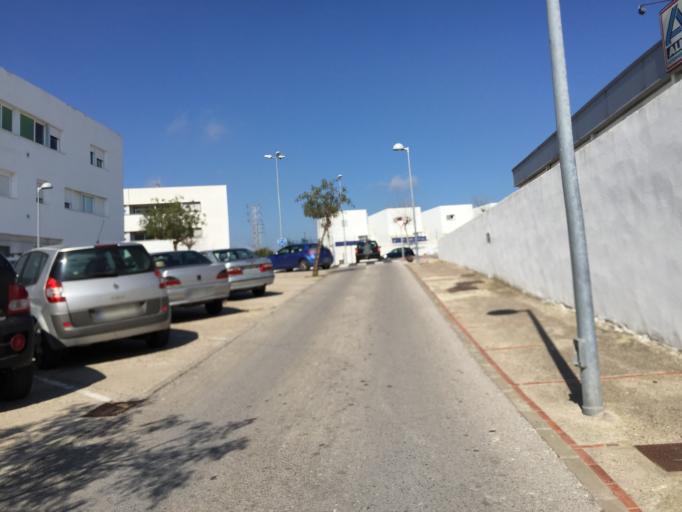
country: ES
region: Andalusia
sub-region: Provincia de Cadiz
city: Conil de la Frontera
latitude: 36.2853
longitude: -6.0795
